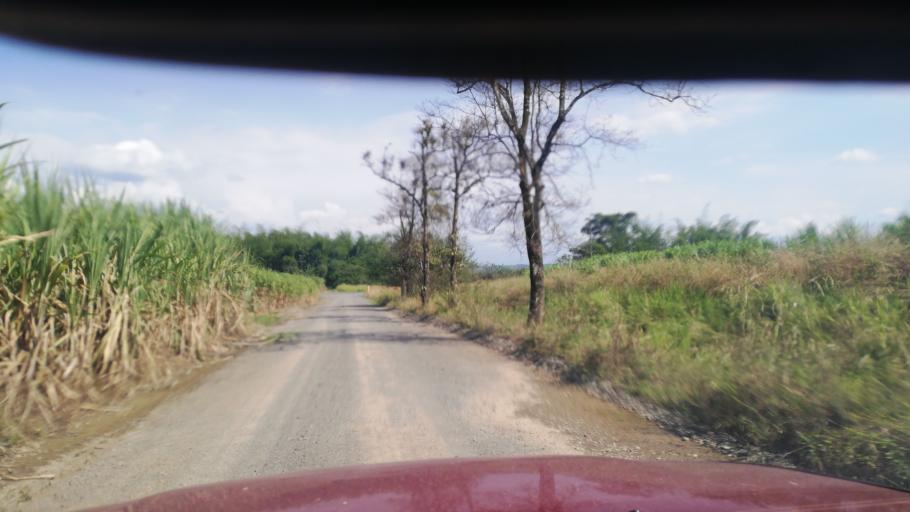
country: CO
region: Risaralda
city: La Virginia
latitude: 4.8876
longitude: -75.9125
